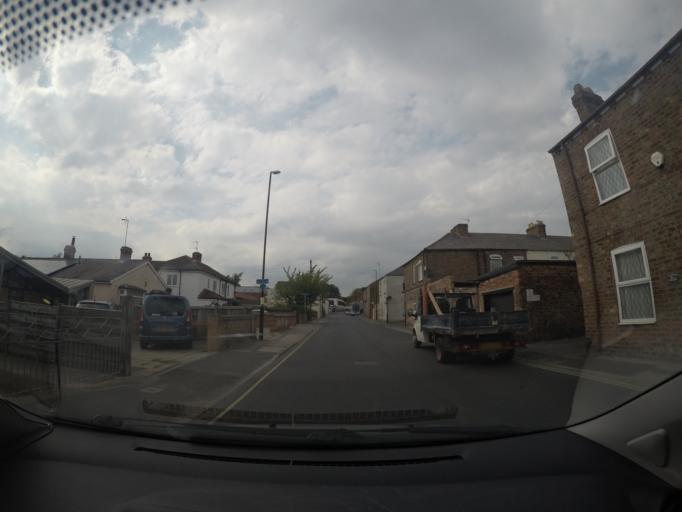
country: GB
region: England
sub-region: City of York
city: York
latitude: 53.9540
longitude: -1.1241
